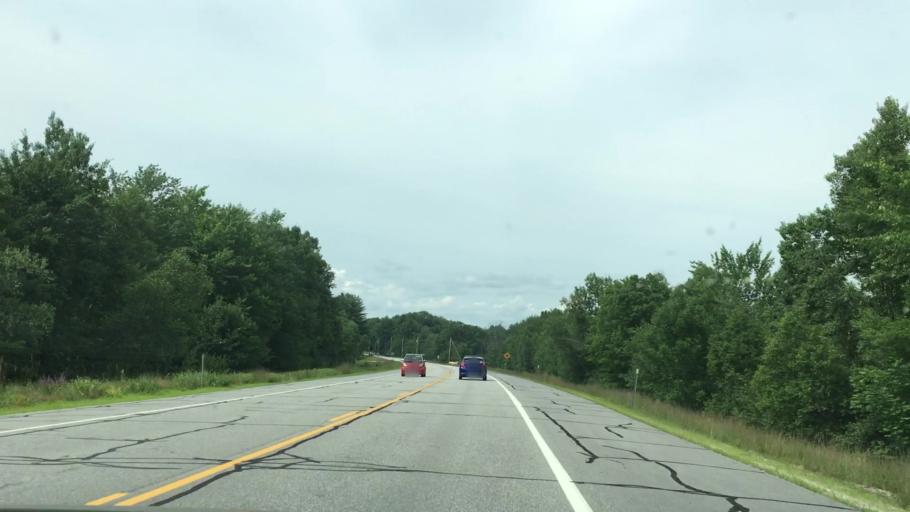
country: US
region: New Hampshire
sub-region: Hillsborough County
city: Hillsborough
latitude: 43.0822
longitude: -71.9173
